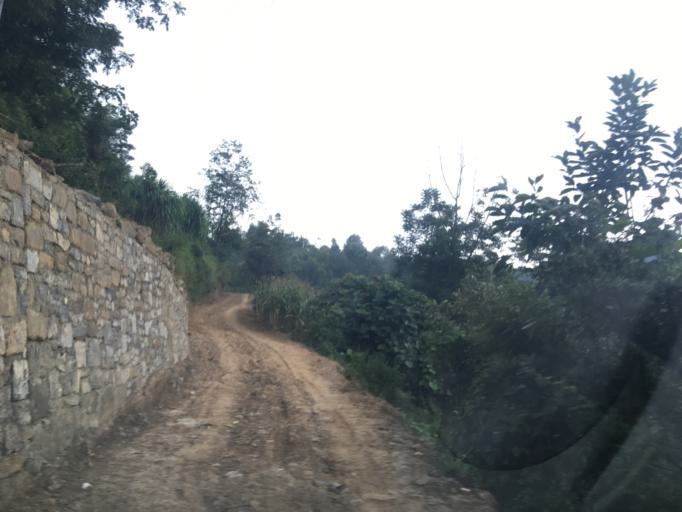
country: CN
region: Guangxi Zhuangzu Zizhiqu
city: Xinzhou
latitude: 25.1629
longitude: 105.6814
